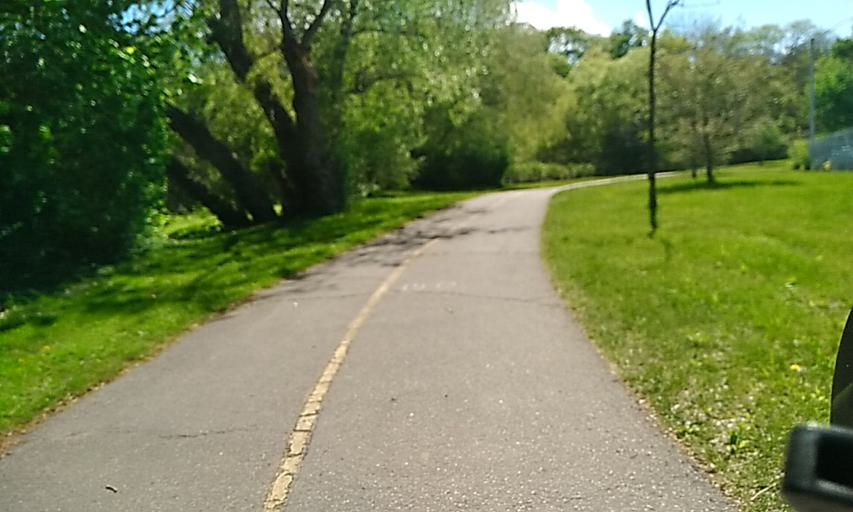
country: CA
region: Ontario
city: London
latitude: 42.9753
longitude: -81.2476
